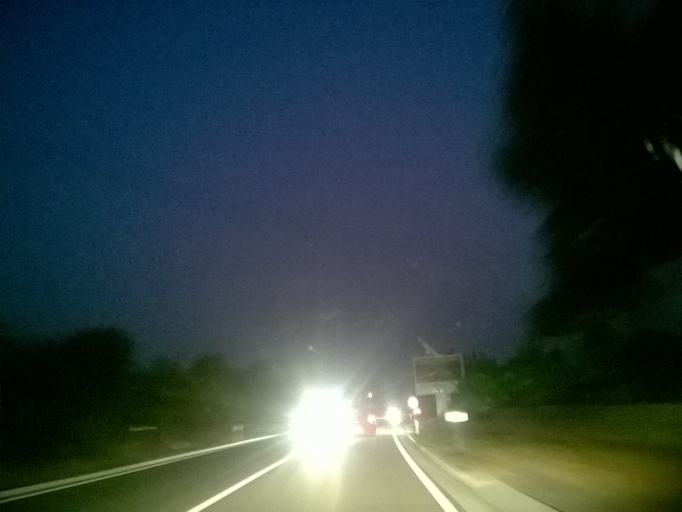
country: ME
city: Mojanovici
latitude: 42.3917
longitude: 19.1294
